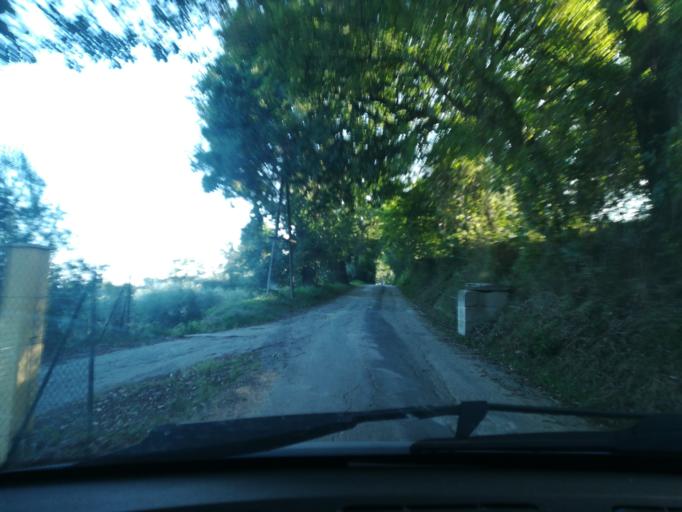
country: IT
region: The Marches
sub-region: Provincia di Macerata
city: Macerata
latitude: 43.2812
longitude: 13.4528
